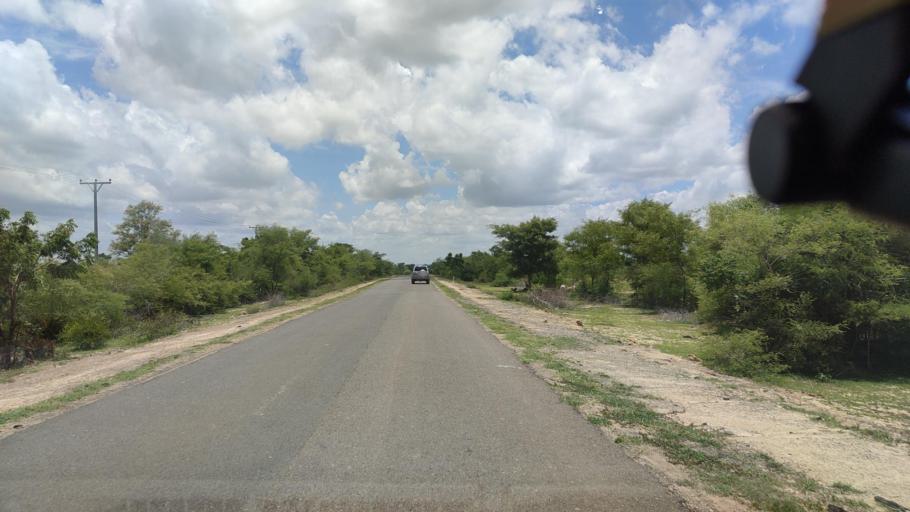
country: MM
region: Magway
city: Taungdwingyi
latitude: 20.1664
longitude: 95.4958
